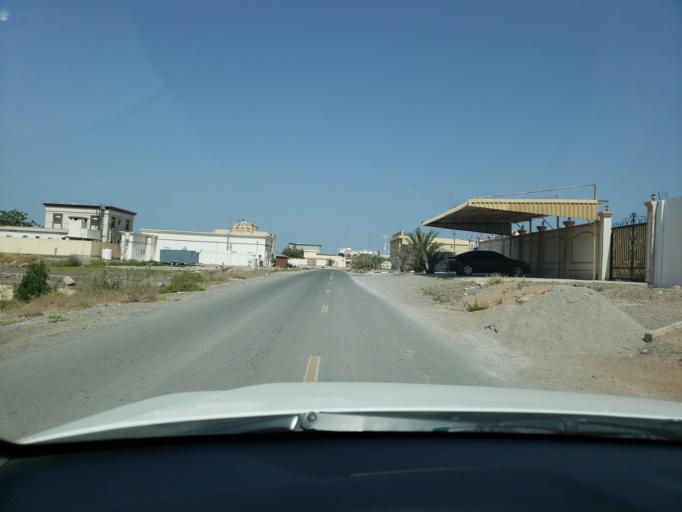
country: AE
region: Ra's al Khaymah
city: Ras al-Khaimah
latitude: 25.8572
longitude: 56.0163
